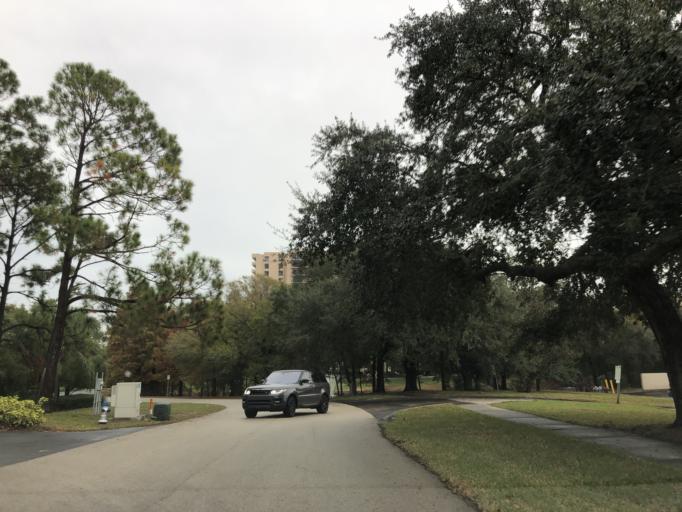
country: US
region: Florida
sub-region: Orange County
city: Doctor Phillips
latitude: 28.4515
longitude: -81.4872
